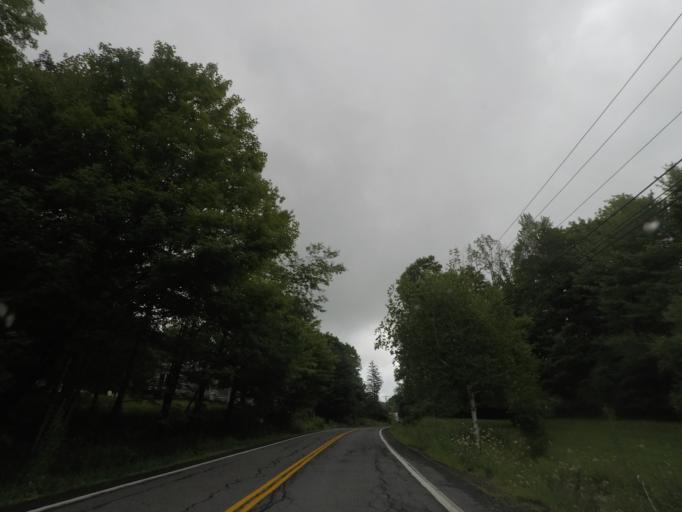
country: US
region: New York
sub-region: Rensselaer County
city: Averill Park
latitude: 42.5823
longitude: -73.4792
